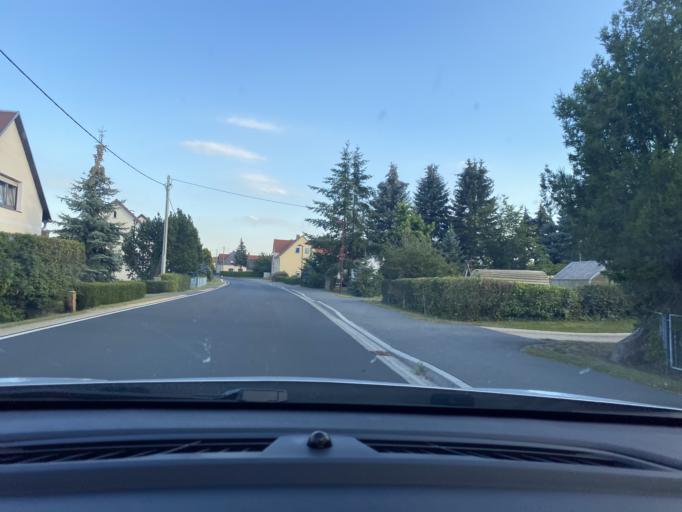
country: DE
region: Saxony
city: Kodersdorf
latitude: 51.2593
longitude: 14.8871
